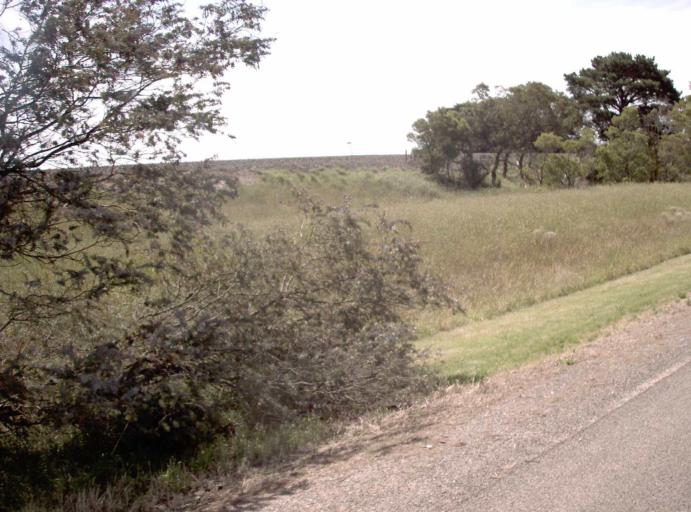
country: AU
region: Victoria
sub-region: Wellington
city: Sale
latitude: -37.9909
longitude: 147.0659
